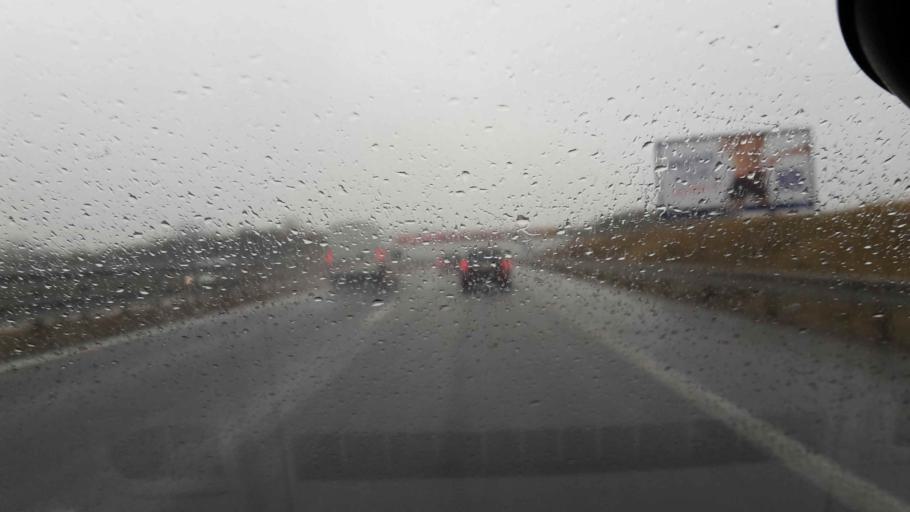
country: CZ
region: South Moravian
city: Podoli
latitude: 49.1869
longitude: 16.7421
